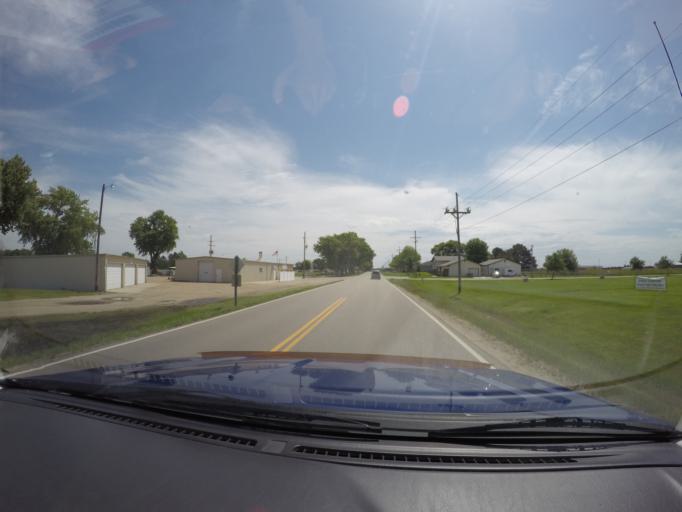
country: US
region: Nebraska
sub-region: Hall County
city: Grand Island
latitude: 40.9024
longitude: -98.3936
